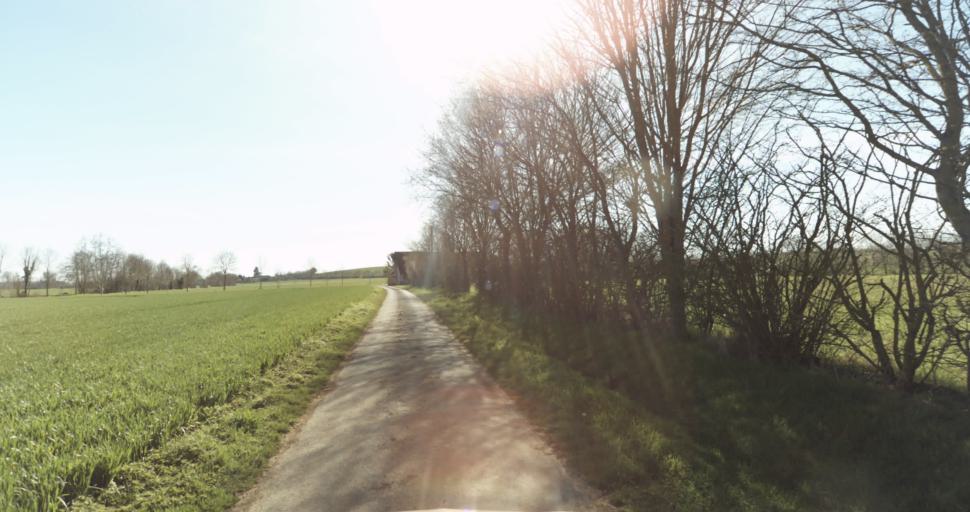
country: FR
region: Lower Normandy
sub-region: Departement du Calvados
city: Saint-Pierre-sur-Dives
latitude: 49.0258
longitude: 0.0196
